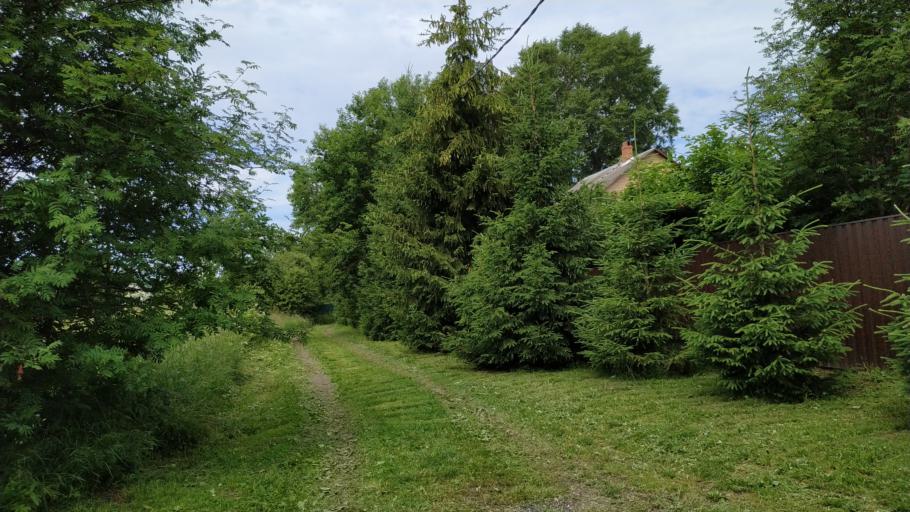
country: RU
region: Moskovskaya
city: Dorokhovo
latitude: 55.5557
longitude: 36.3199
